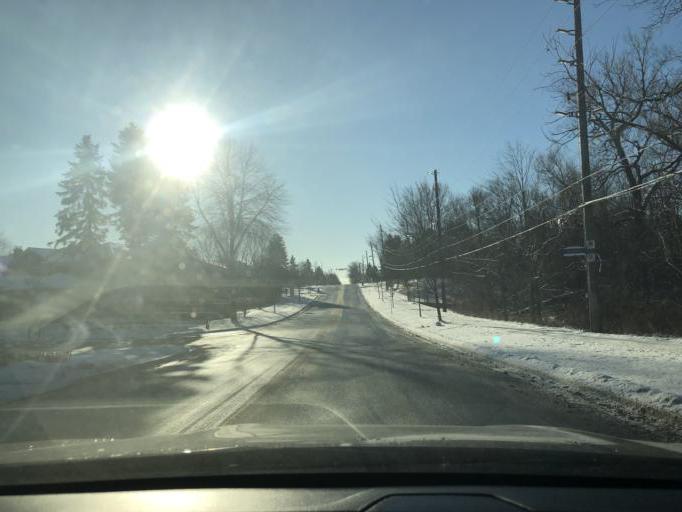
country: CA
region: Ontario
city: Pickering
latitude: 43.7867
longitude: -79.1341
